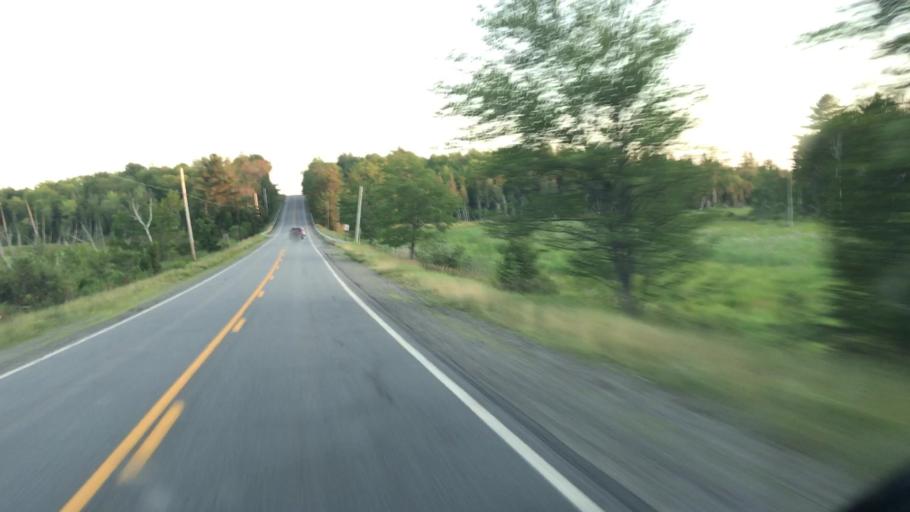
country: US
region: Maine
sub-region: Penobscot County
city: Medway
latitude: 45.5992
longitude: -68.3099
